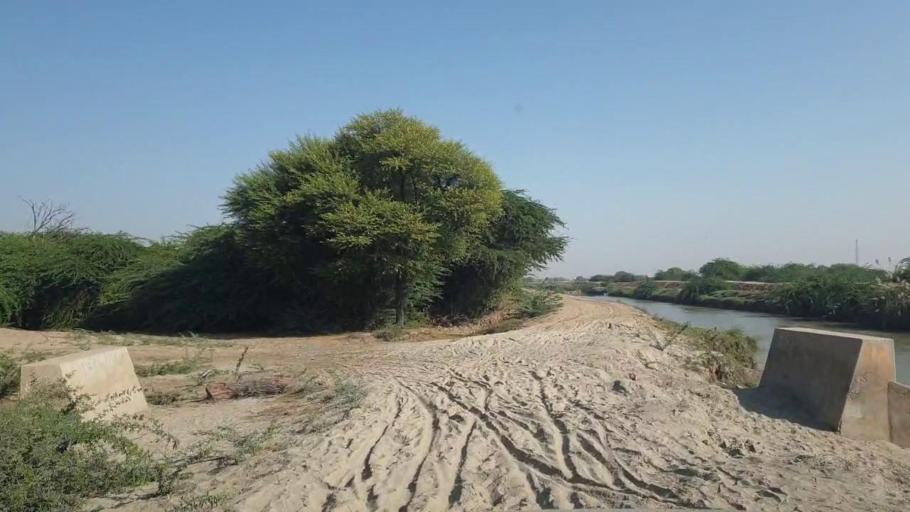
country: PK
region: Sindh
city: Badin
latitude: 24.7242
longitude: 68.8030
